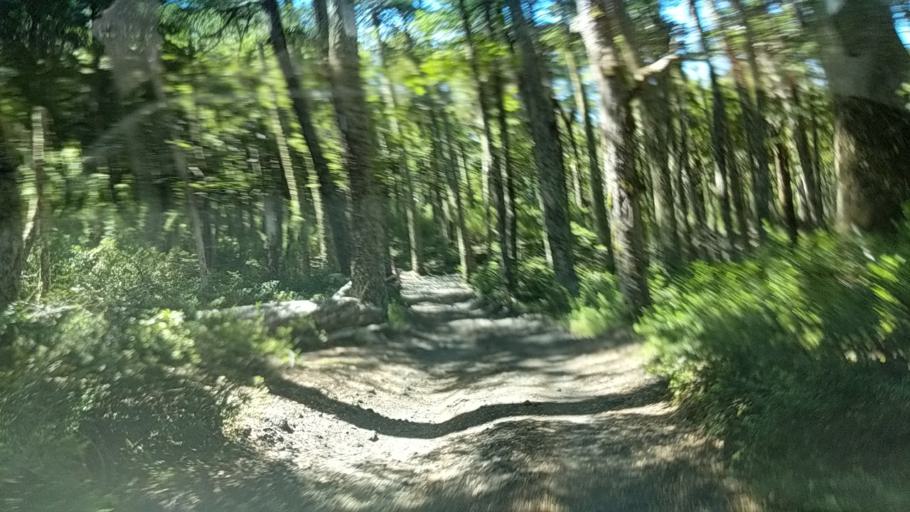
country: CL
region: Araucania
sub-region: Provincia de Cautin
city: Pucon
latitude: -39.4664
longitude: -71.8530
